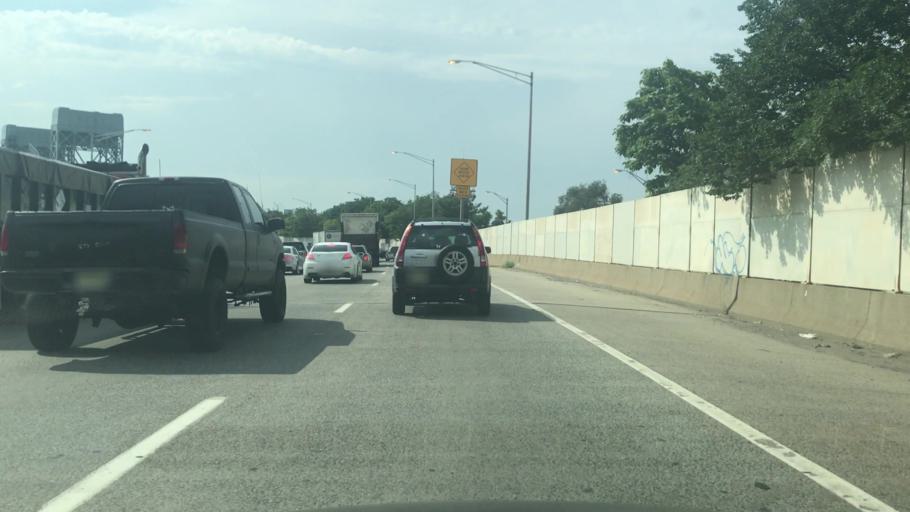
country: US
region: New Jersey
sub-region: Hudson County
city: East Newark
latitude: 40.7466
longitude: -74.1613
